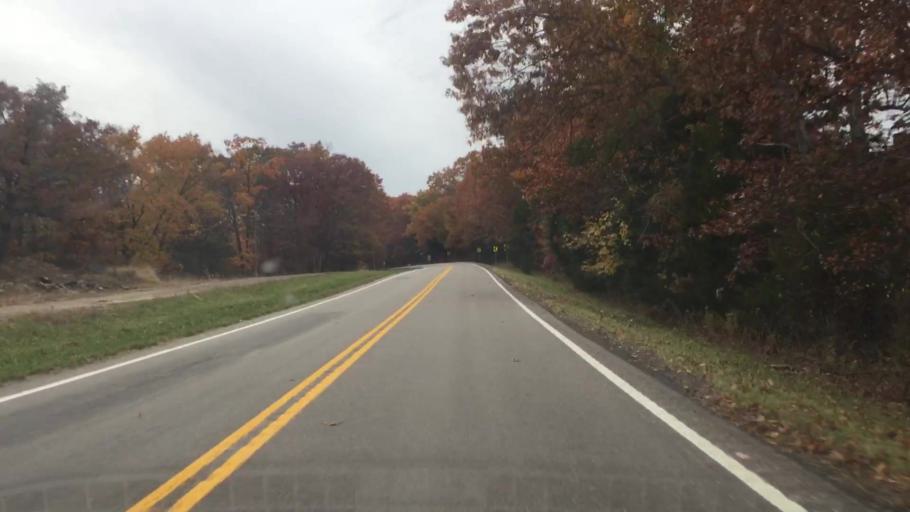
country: US
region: Missouri
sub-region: Gasconade County
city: Hermann
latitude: 38.7198
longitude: -91.6707
